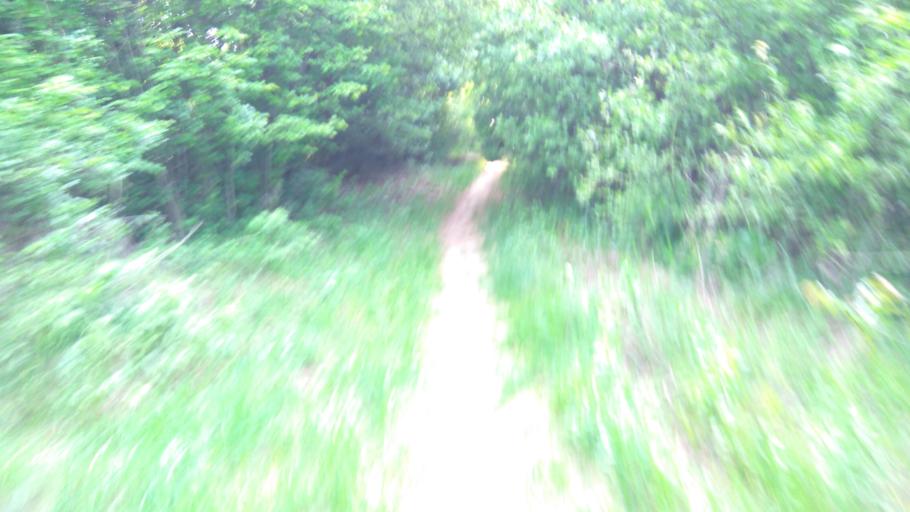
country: HU
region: Pest
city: Csobanka
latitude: 47.6520
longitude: 18.9834
